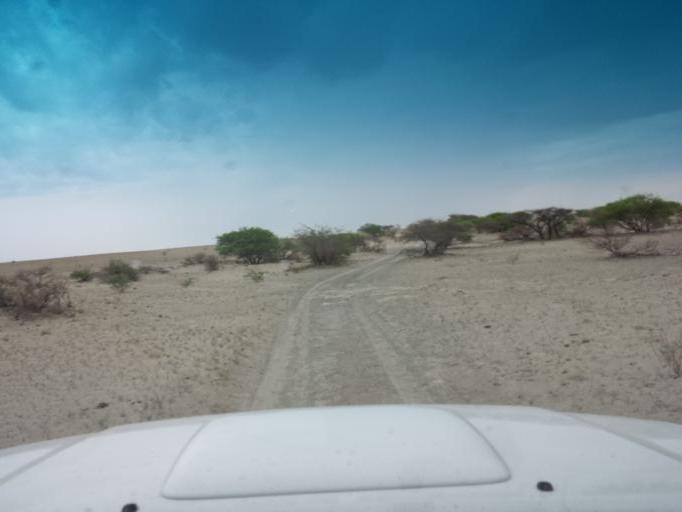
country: BW
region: Central
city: Mopipi
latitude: -21.1684
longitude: 24.8745
